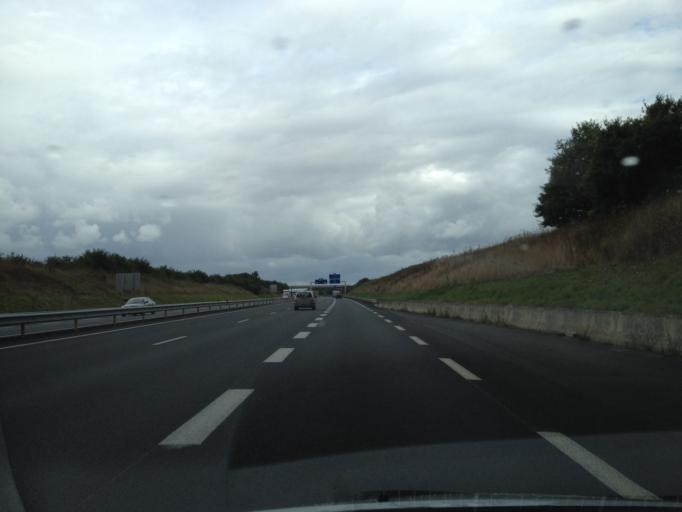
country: FR
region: Pays de la Loire
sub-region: Departement de la Vendee
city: Les Essarts
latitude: 46.8006
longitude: -1.2025
